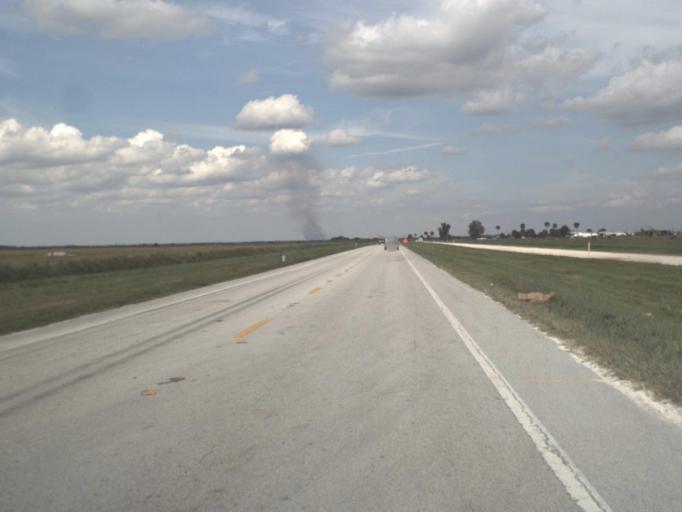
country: US
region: Florida
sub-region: Okeechobee County
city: Cypress Quarters
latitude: 27.4347
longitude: -80.8117
